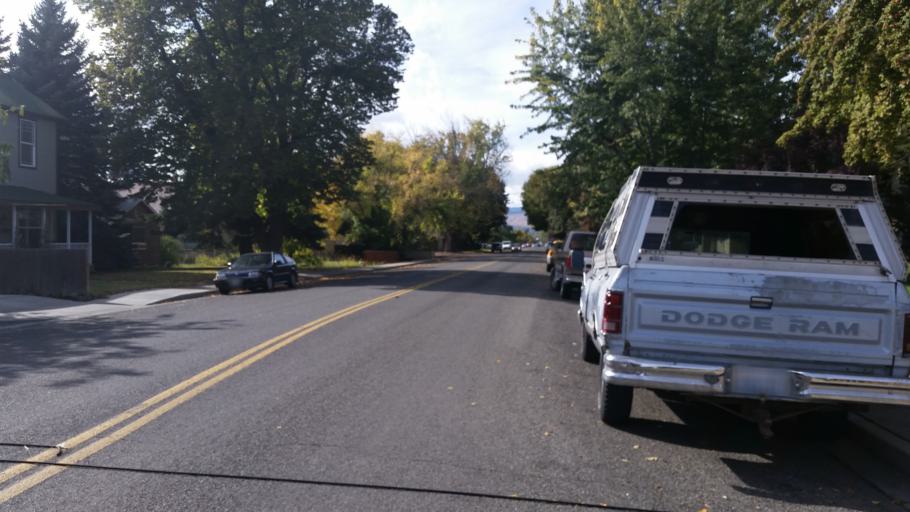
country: US
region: Washington
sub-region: Kittitas County
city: Ellensburg
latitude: 46.9968
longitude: -120.5378
